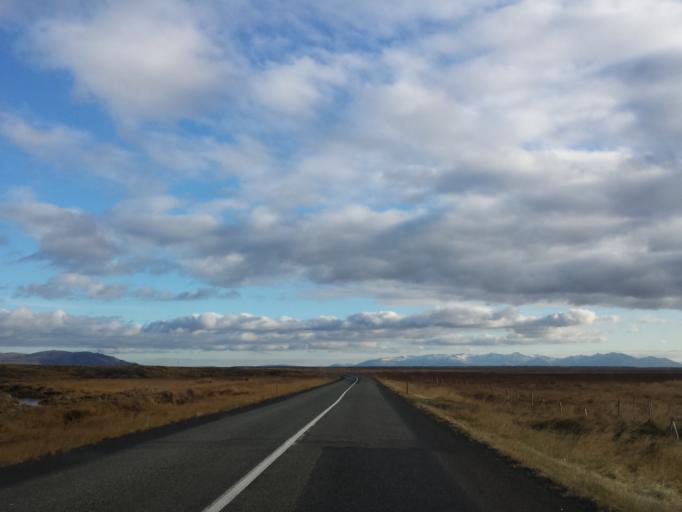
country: IS
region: West
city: Borgarnes
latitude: 64.7435
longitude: -22.2239
